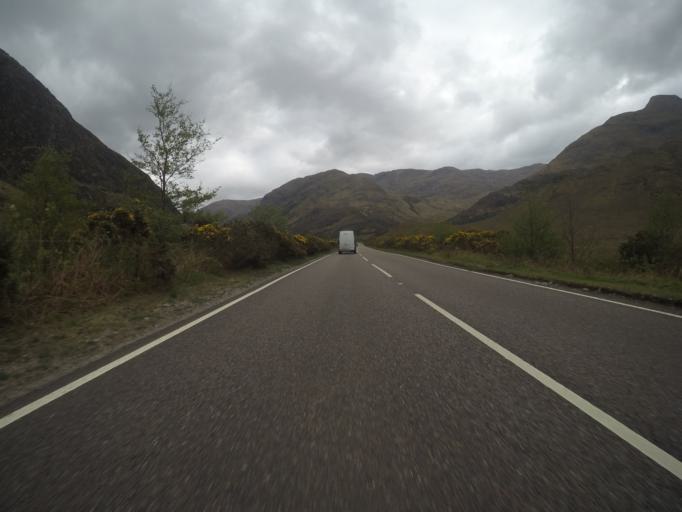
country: GB
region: Scotland
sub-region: Highland
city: Fort William
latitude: 57.1751
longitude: -5.3632
